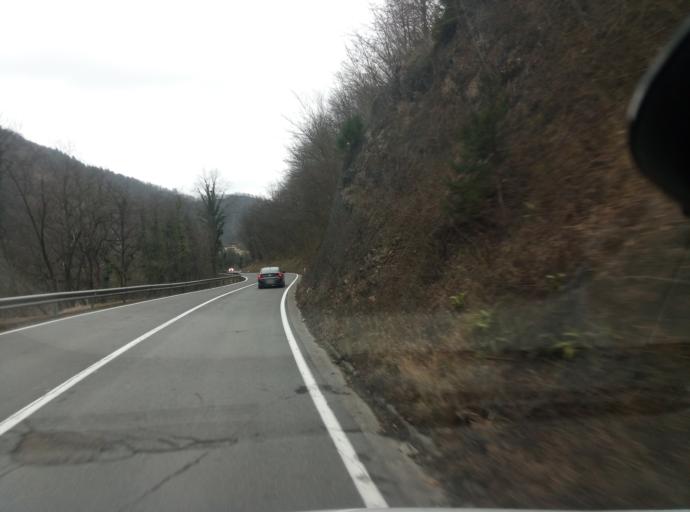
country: SI
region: Zagorje ob Savi
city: Zagorje ob Savi
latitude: 46.1155
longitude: 14.9850
